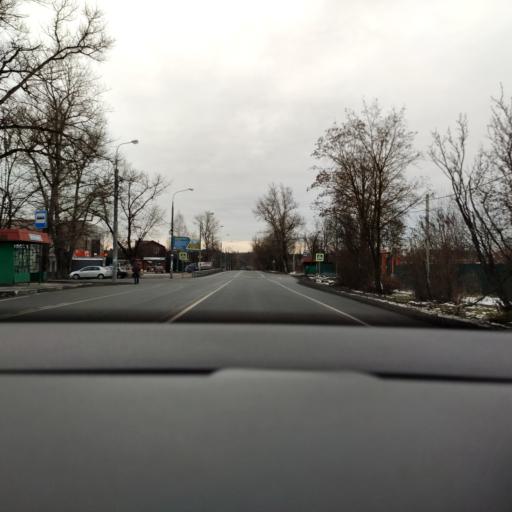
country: RU
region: Moskovskaya
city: Zvenigorod
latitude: 55.7226
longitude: 36.8635
